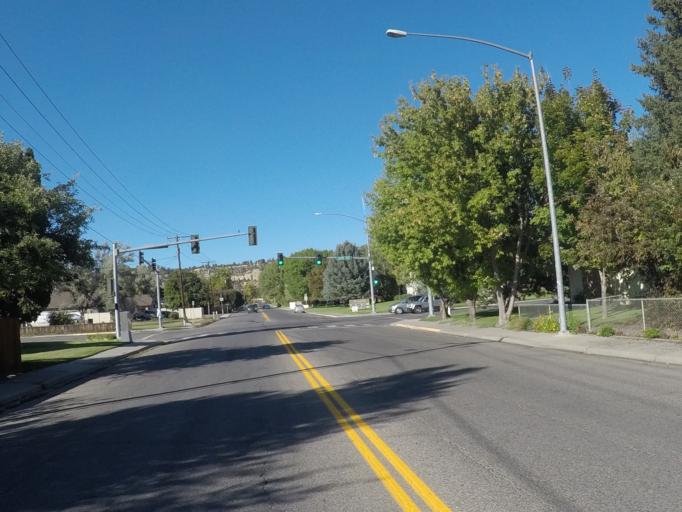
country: US
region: Montana
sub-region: Yellowstone County
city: Billings
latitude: 45.7909
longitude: -108.5904
